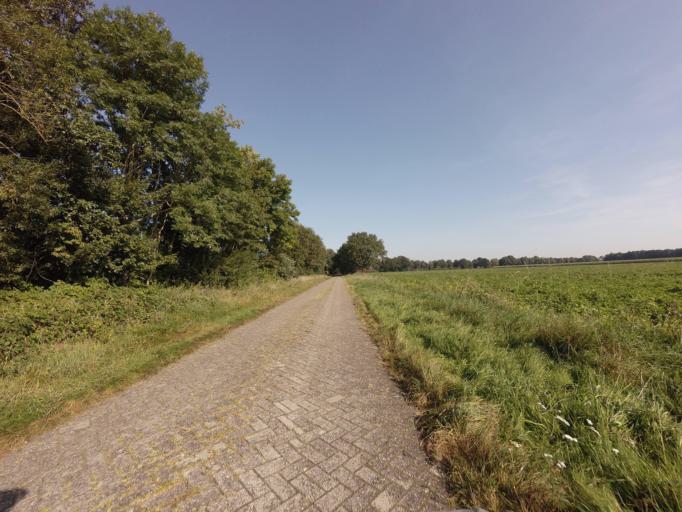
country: DE
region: Lower Saxony
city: Laar
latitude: 52.5927
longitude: 6.7792
